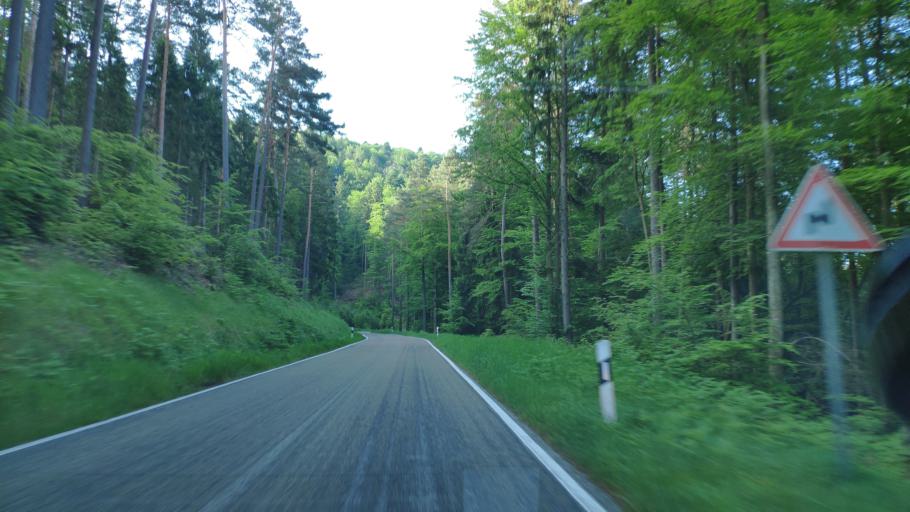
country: DE
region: Rheinland-Pfalz
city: Lemberg
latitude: 49.1366
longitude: 7.6897
